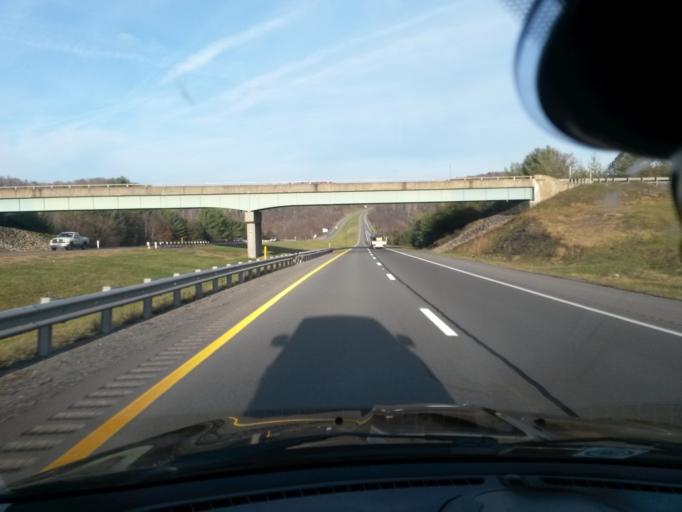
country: US
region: West Virginia
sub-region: Greenbrier County
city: Lewisburg
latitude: 37.8678
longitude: -80.5530
